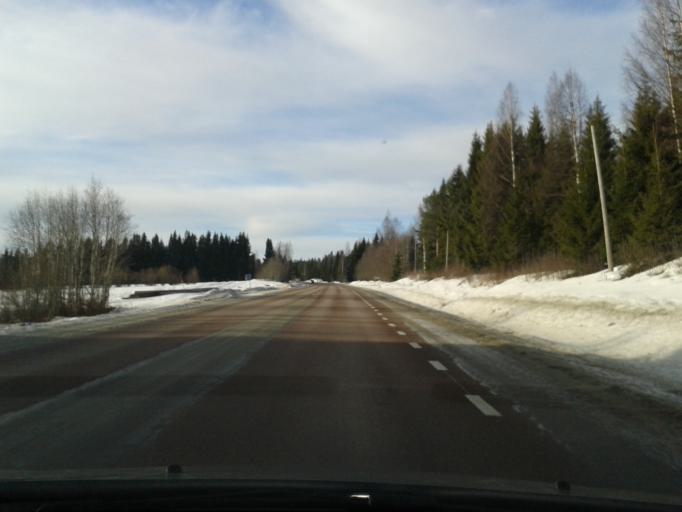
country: SE
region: Vaesternorrland
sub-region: OErnskoeldsviks Kommun
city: Bredbyn
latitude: 63.3938
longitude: 18.3303
